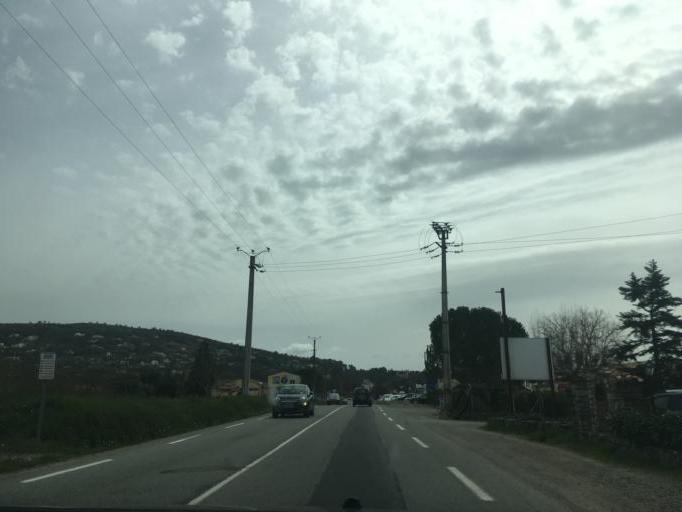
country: FR
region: Provence-Alpes-Cote d'Azur
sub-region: Departement du Var
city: Montauroux
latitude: 43.6033
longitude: 6.7746
